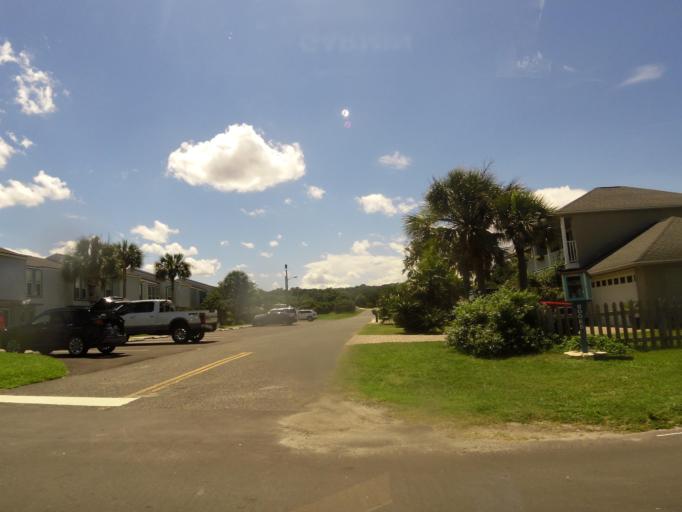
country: US
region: Florida
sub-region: Nassau County
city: Fernandina Beach
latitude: 30.6758
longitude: -81.4313
